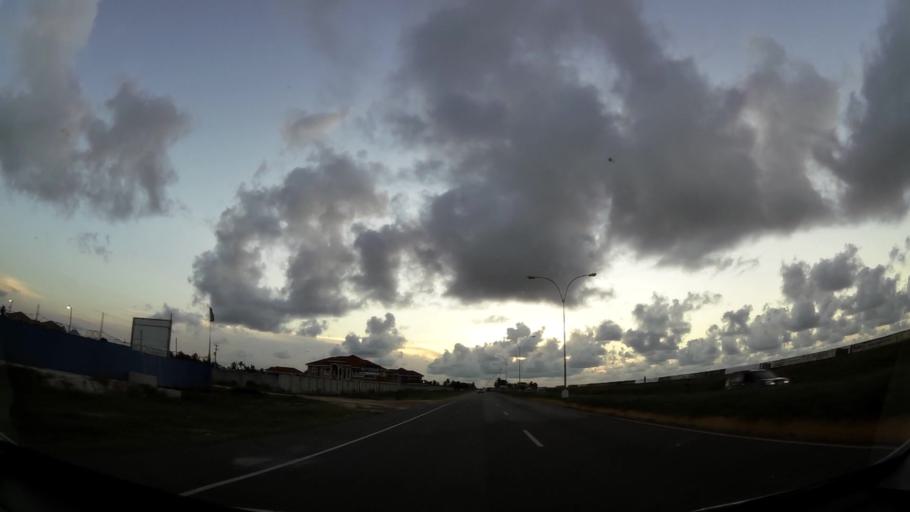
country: GY
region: Demerara-Mahaica
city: Georgetown
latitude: 6.8252
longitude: -58.1144
